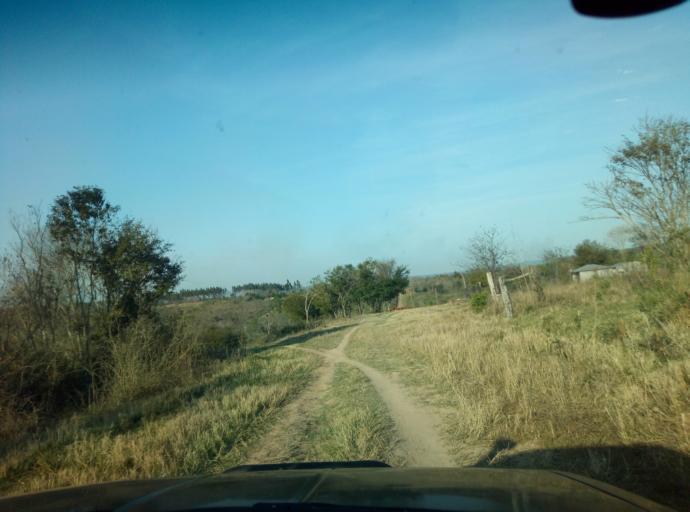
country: PY
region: Caaguazu
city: Doctor Cecilio Baez
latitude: -25.2000
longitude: -56.1280
